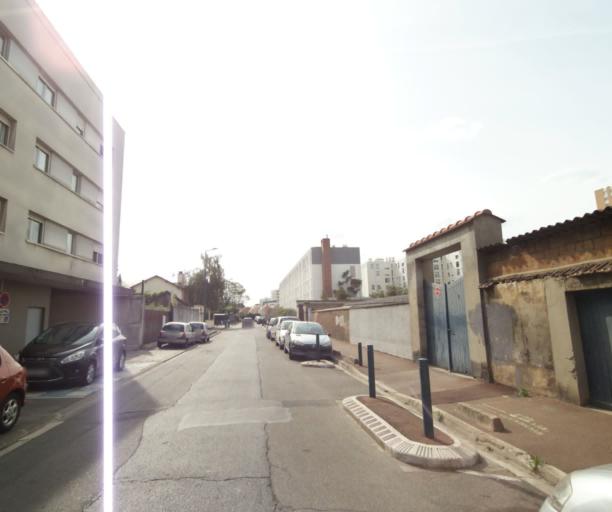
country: FR
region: Ile-de-France
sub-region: Departement des Hauts-de-Seine
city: Gennevilliers
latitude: 48.9317
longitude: 2.2943
